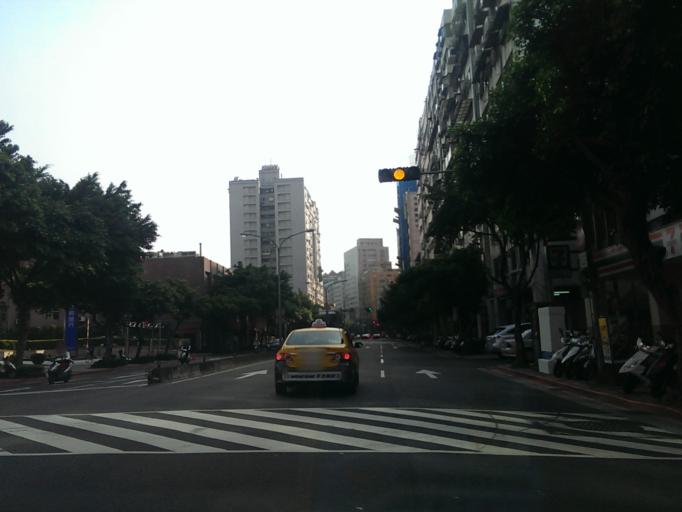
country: TW
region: Taipei
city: Taipei
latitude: 25.0257
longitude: 121.5542
